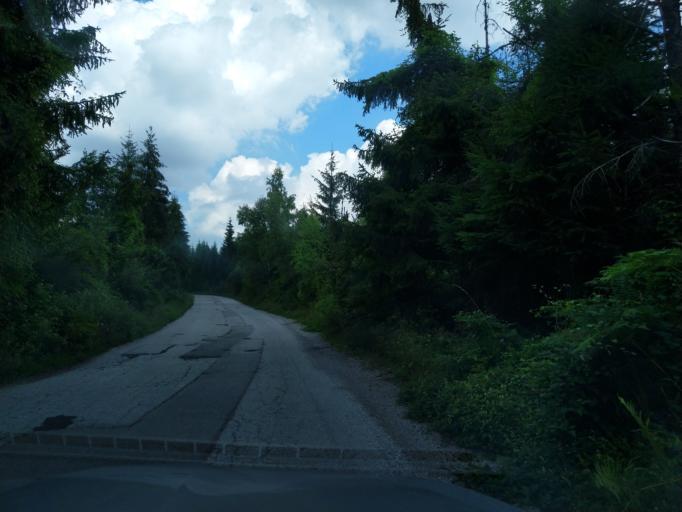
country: RS
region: Central Serbia
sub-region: Zlatiborski Okrug
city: Nova Varos
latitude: 43.5279
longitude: 19.8847
